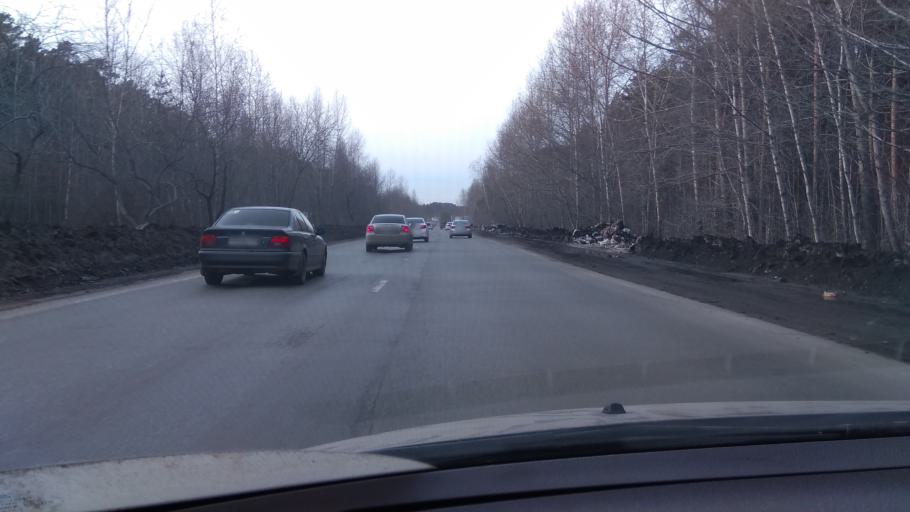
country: RU
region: Sverdlovsk
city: Shirokaya Rechka
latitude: 56.8087
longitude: 60.5281
